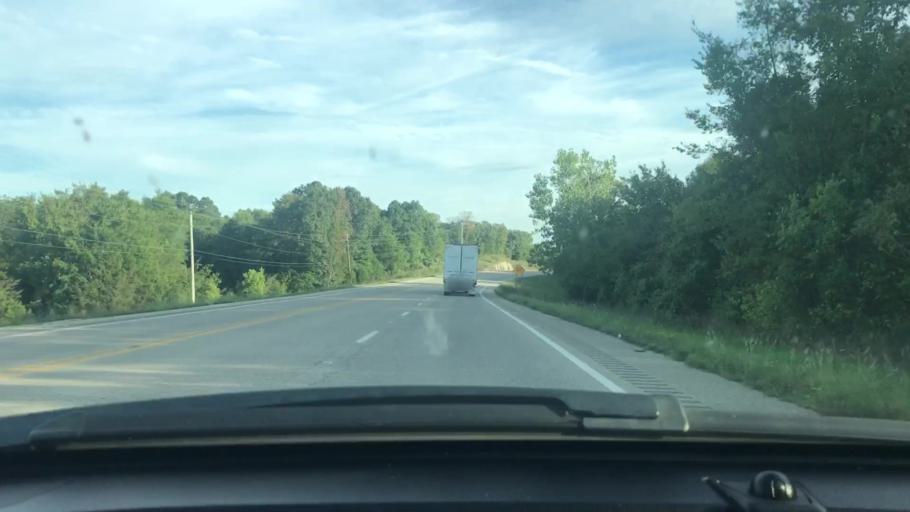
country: US
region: Arkansas
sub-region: Randolph County
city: Pocahontas
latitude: 36.1890
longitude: -91.1636
